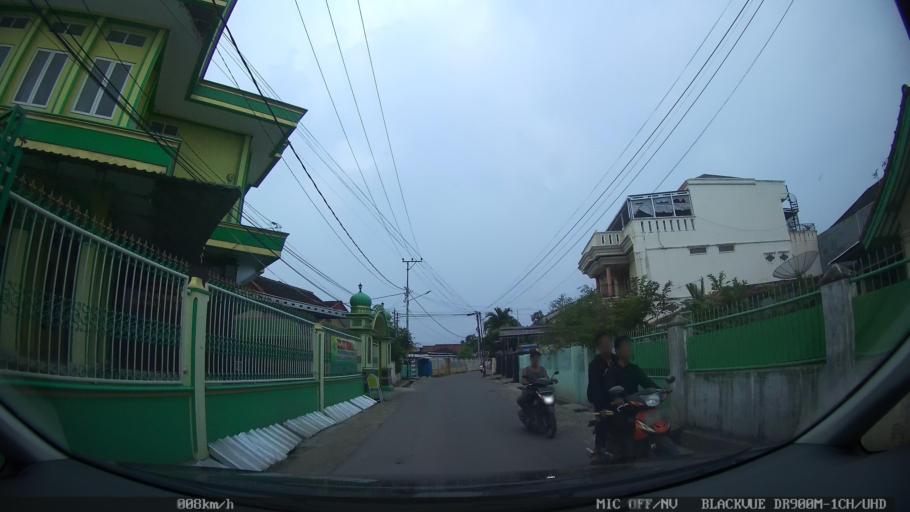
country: ID
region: Lampung
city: Kedaton
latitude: -5.4042
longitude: 105.2674
